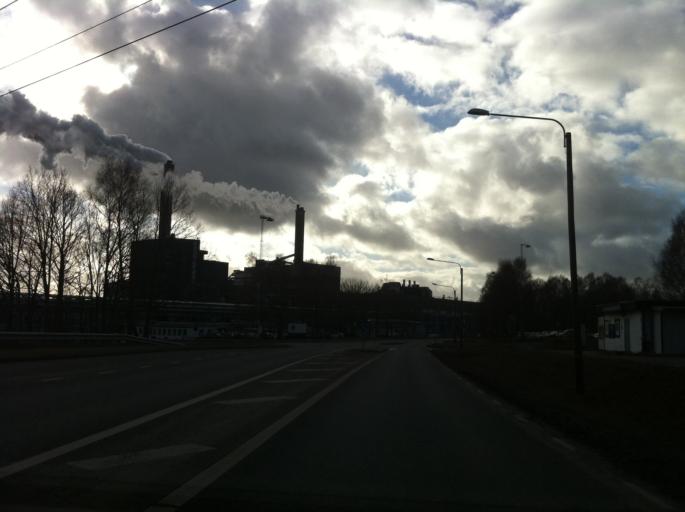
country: SE
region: Blekinge
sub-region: Solvesborgs Kommun
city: Soelvesborg
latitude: 56.0631
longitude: 14.5363
